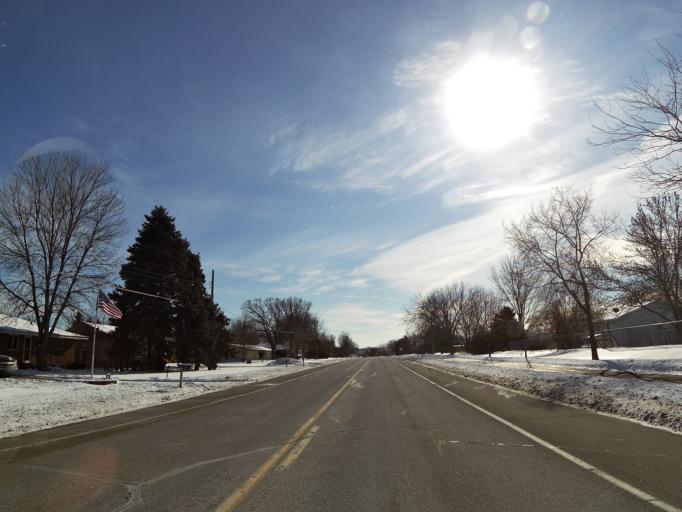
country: US
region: Minnesota
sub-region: Dakota County
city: Hastings
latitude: 44.7534
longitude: -92.8821
